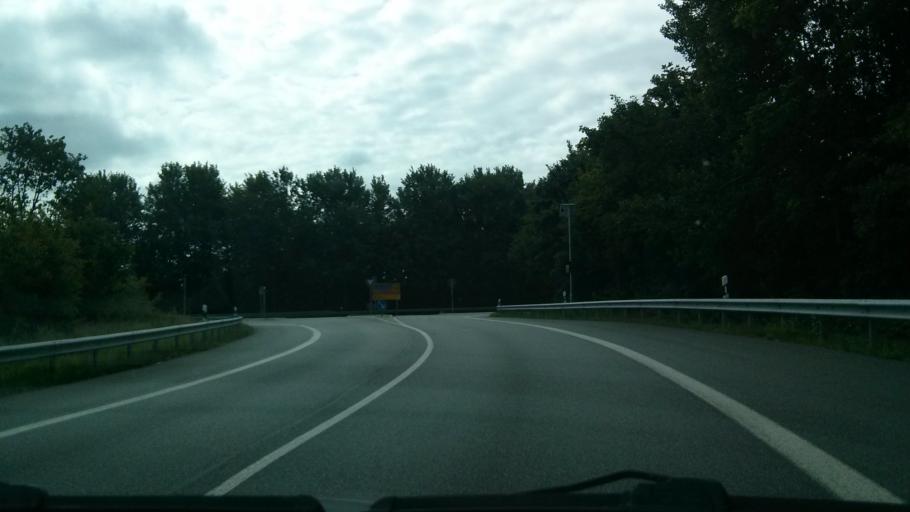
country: DE
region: Lower Saxony
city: Driftsethe
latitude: 53.4420
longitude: 8.5811
